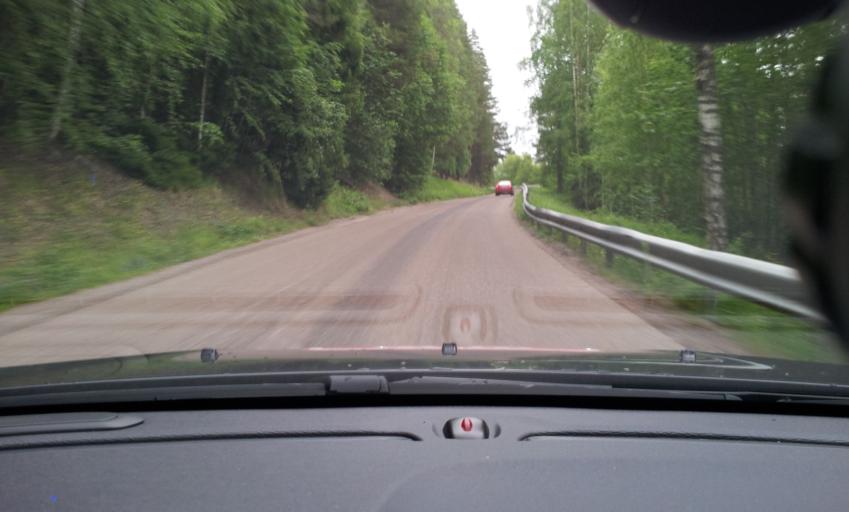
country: SE
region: Jaemtland
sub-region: Ragunda Kommun
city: Hammarstrand
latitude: 63.0117
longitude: 16.6374
